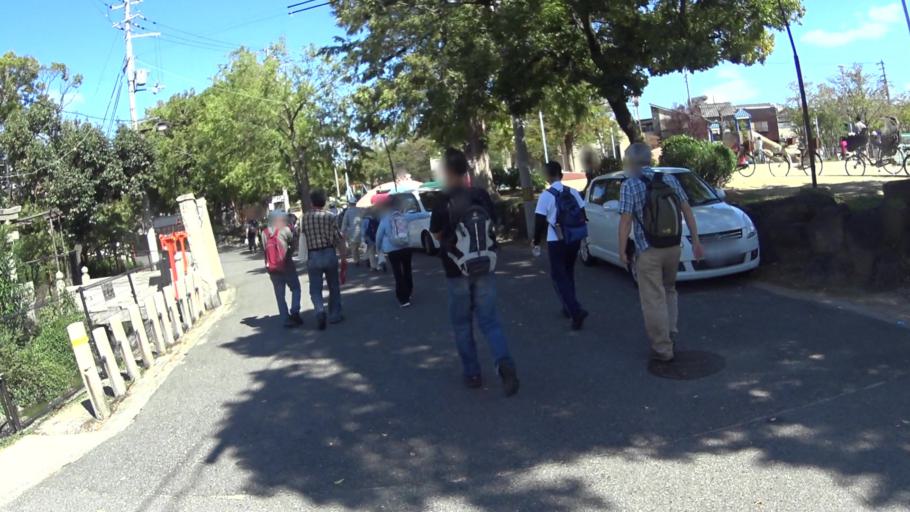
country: JP
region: Osaka
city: Yao
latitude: 34.6267
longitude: 135.5551
